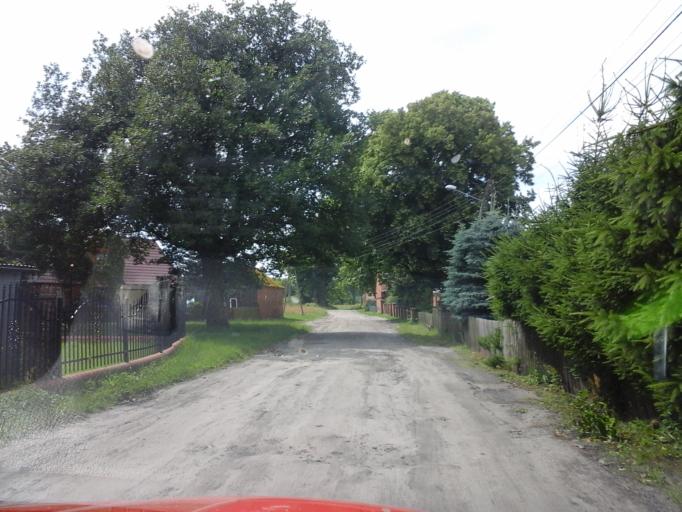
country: PL
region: Lubusz
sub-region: Powiat strzelecko-drezdenecki
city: Dobiegniew
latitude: 53.0780
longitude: 15.7847
